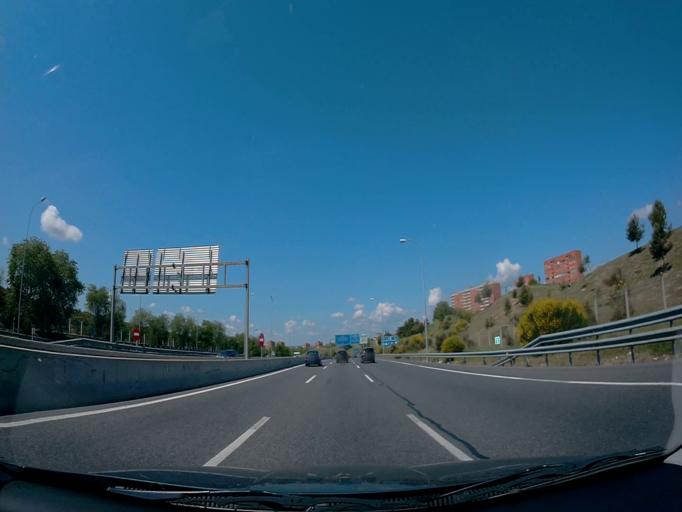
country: ES
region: Madrid
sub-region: Provincia de Madrid
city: Puente de Vallecas
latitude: 40.3786
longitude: -3.6460
